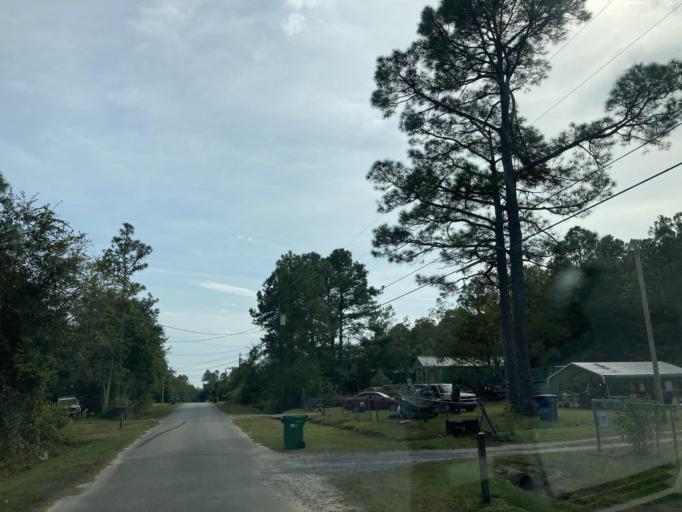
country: US
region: Mississippi
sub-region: Jackson County
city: Saint Martin
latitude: 30.4783
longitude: -88.8464
